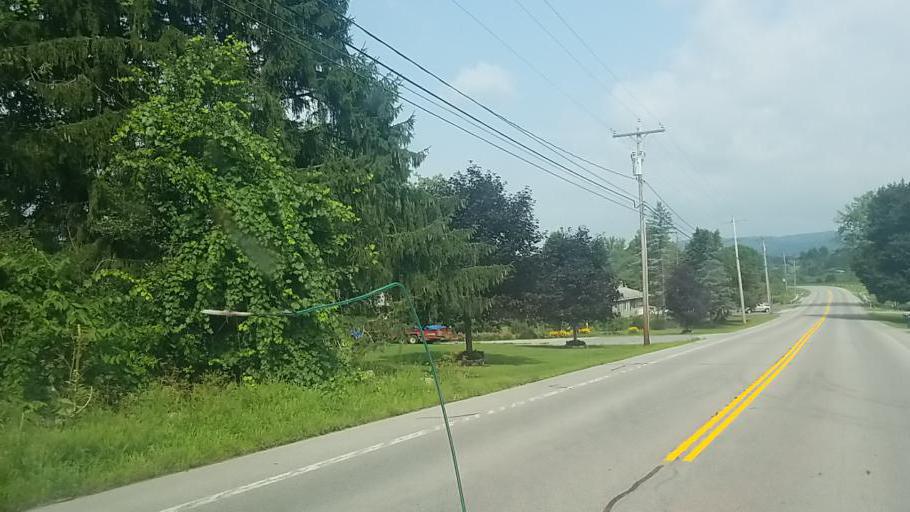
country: US
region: New York
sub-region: Montgomery County
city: Fort Plain
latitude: 42.9542
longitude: -74.6210
